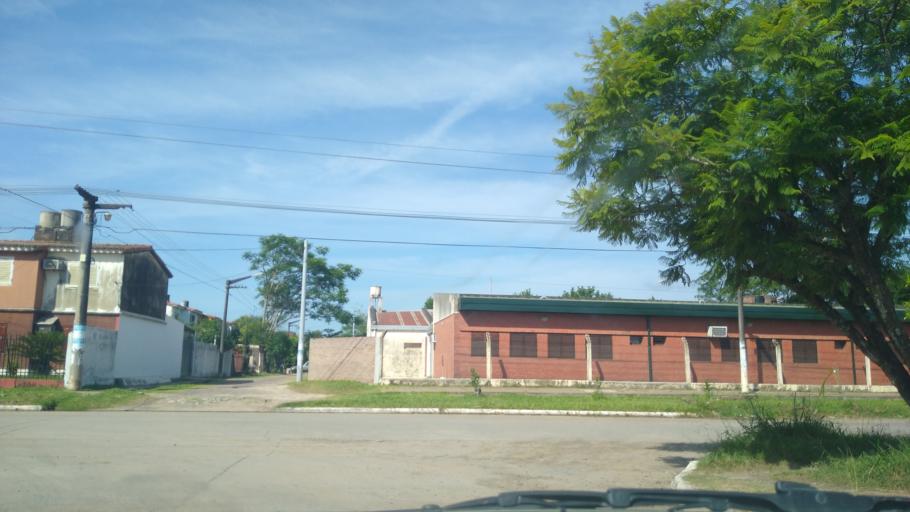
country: AR
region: Chaco
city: Puerto Vilelas
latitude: -27.4974
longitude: -58.9541
